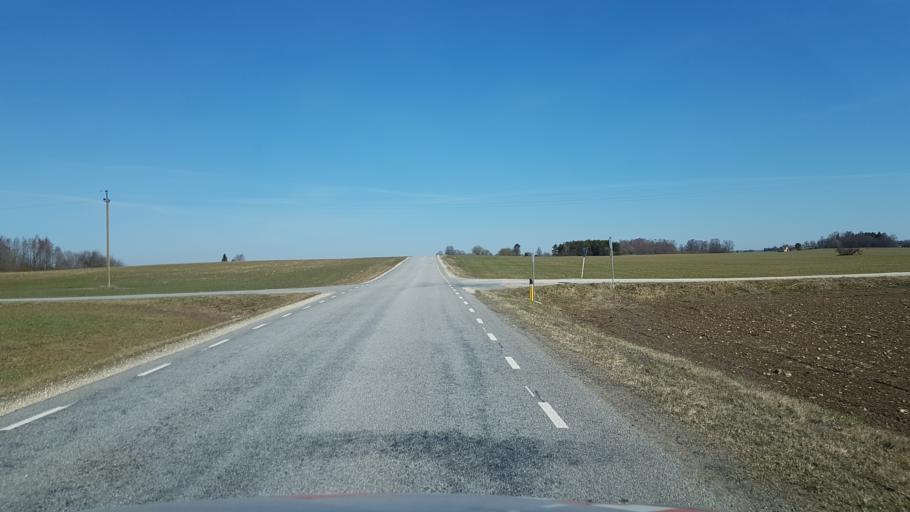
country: EE
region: Laeaene-Virumaa
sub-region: Vinni vald
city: Vinni
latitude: 59.2706
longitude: 26.3718
